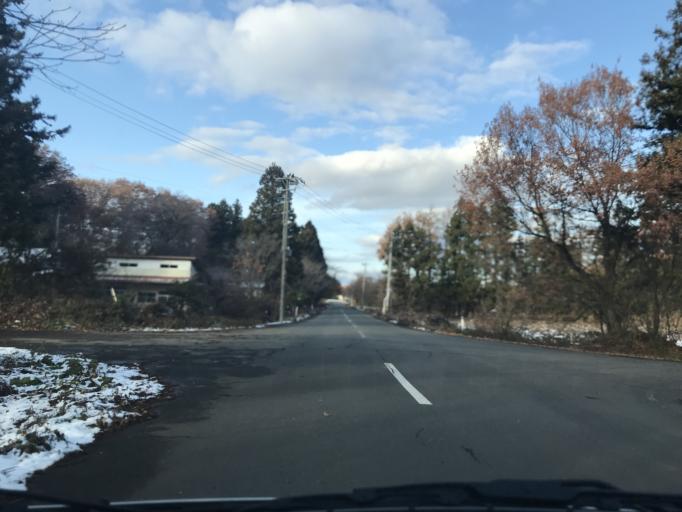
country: JP
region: Iwate
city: Kitakami
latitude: 39.2522
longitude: 141.0325
